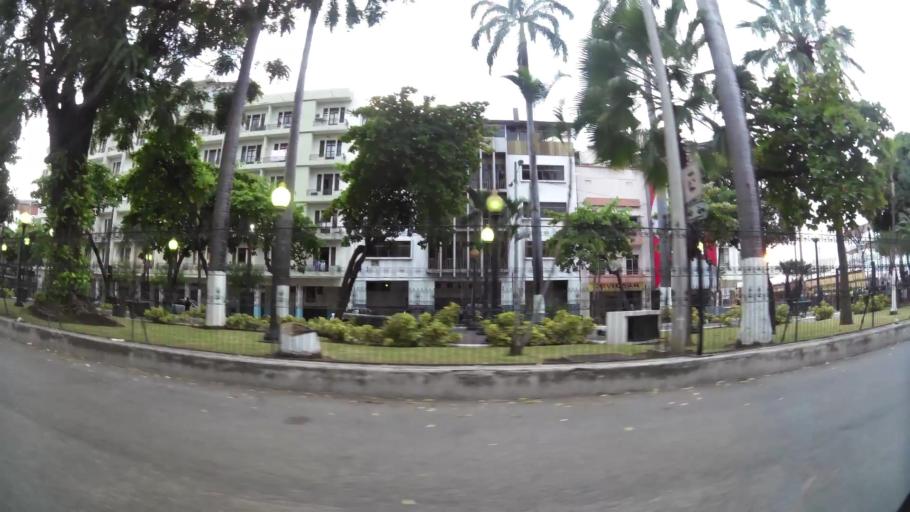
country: EC
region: Guayas
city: Guayaquil
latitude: -2.2006
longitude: -79.8826
